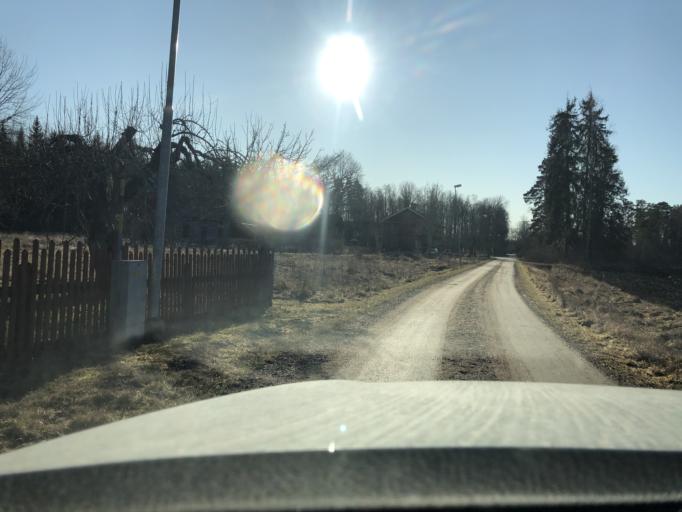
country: SE
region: Uppsala
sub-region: Heby Kommun
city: Tarnsjo
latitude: 60.2948
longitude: 16.8880
